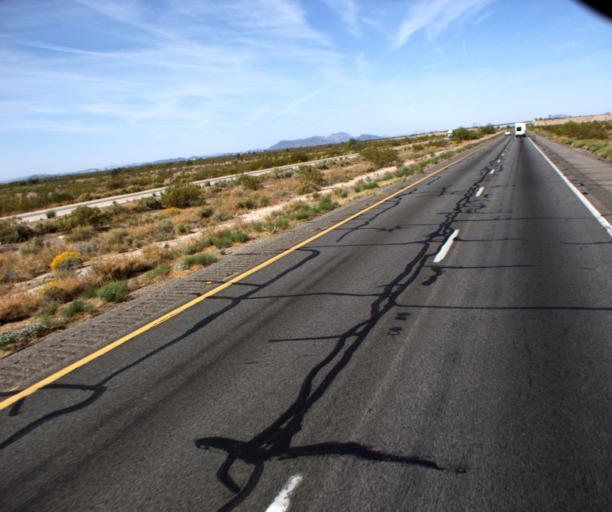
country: US
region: Arizona
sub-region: Maricopa County
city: Buckeye
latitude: 33.4451
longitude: -112.7025
